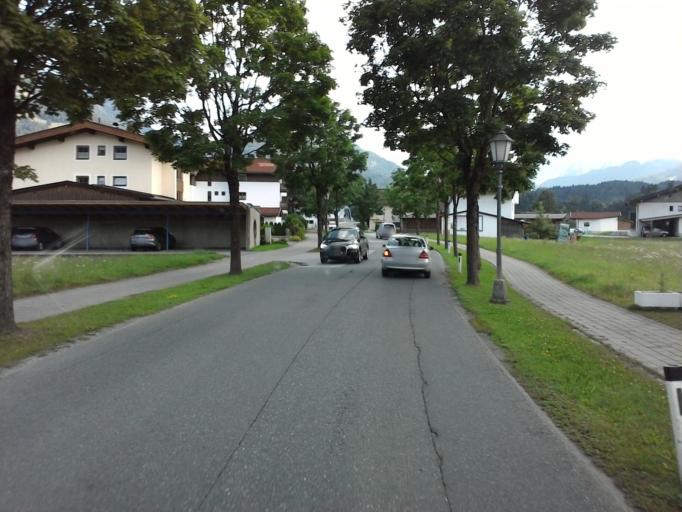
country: AT
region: Tyrol
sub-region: Politischer Bezirk Kitzbuhel
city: Kossen
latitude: 47.6631
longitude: 12.4044
